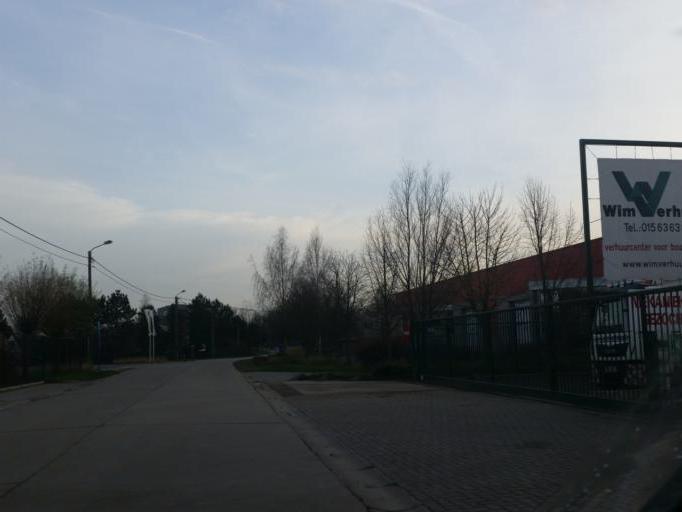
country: BE
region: Flanders
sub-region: Provincie Antwerpen
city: Sint-Katelijne-Waver
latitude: 51.0641
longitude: 4.5094
